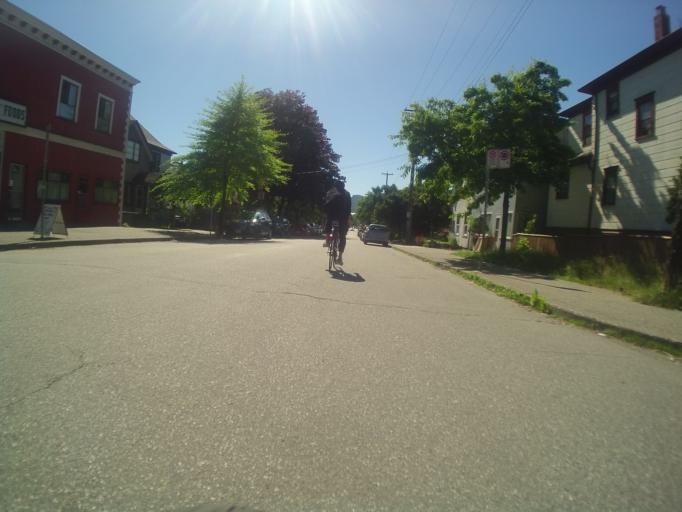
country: CA
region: British Columbia
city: Vancouver
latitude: 49.2775
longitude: -123.0916
